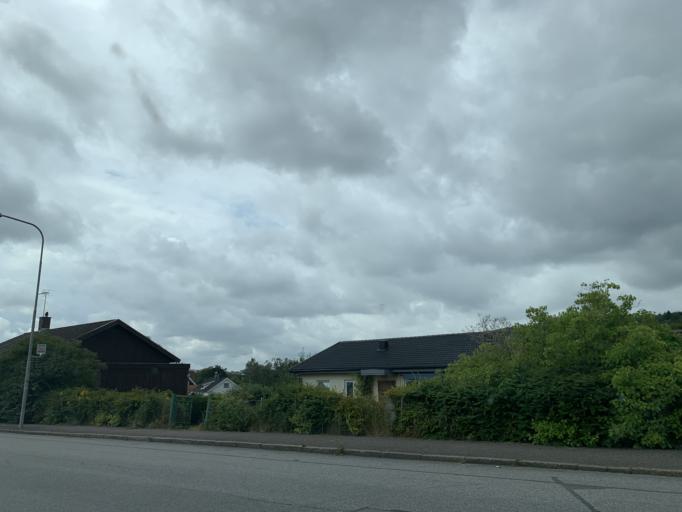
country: SE
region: Vaestra Goetaland
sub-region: Goteborg
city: Eriksbo
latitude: 57.7430
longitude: 12.0498
